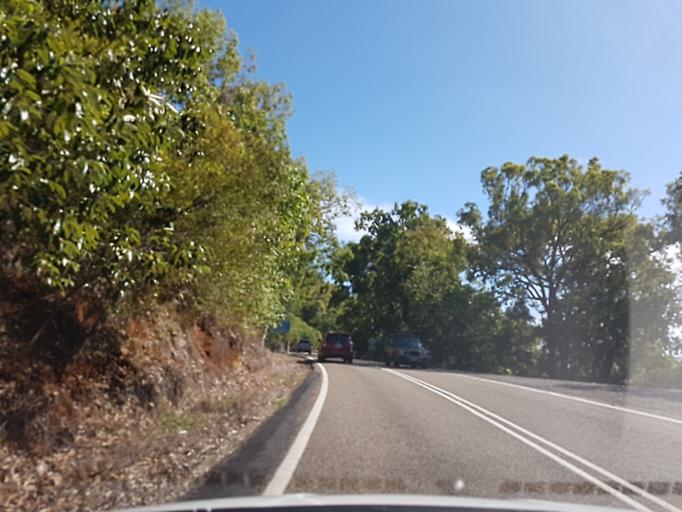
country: AU
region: Queensland
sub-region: Cairns
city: Port Douglas
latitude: -16.6063
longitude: 145.5278
